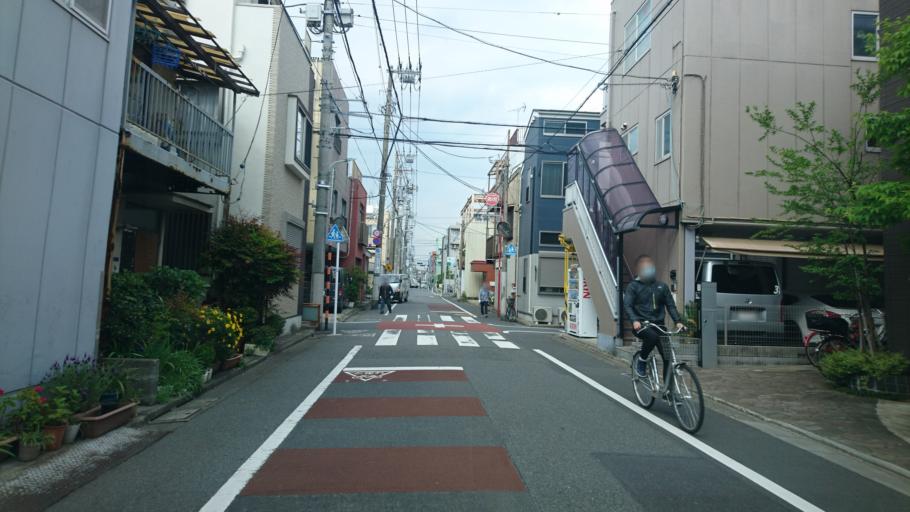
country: JP
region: Kanagawa
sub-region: Kawasaki-shi
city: Kawasaki
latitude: 35.5490
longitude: 139.7193
